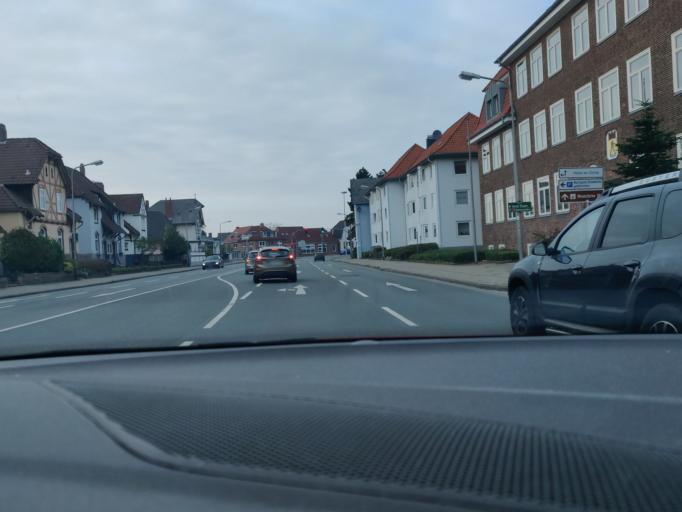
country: DE
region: Lower Saxony
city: Cuxhaven
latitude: 53.8558
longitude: 8.7066
